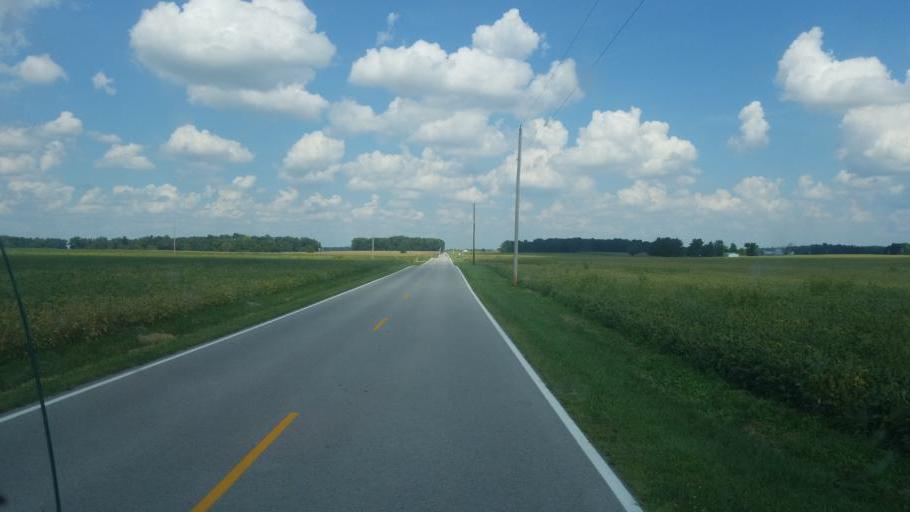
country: US
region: Ohio
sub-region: Hancock County
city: Arlington
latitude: 40.8559
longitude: -83.7276
